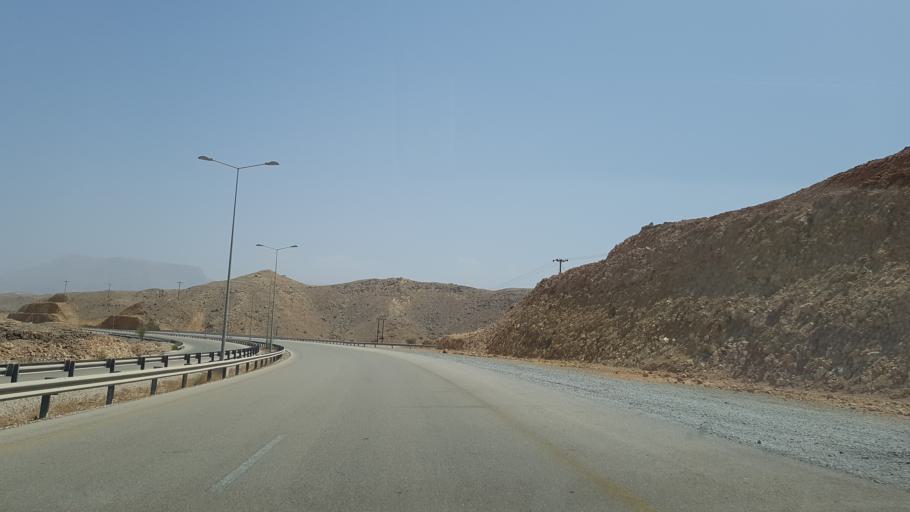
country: OM
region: Muhafazat Masqat
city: Muscat
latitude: 23.1423
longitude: 58.9677
